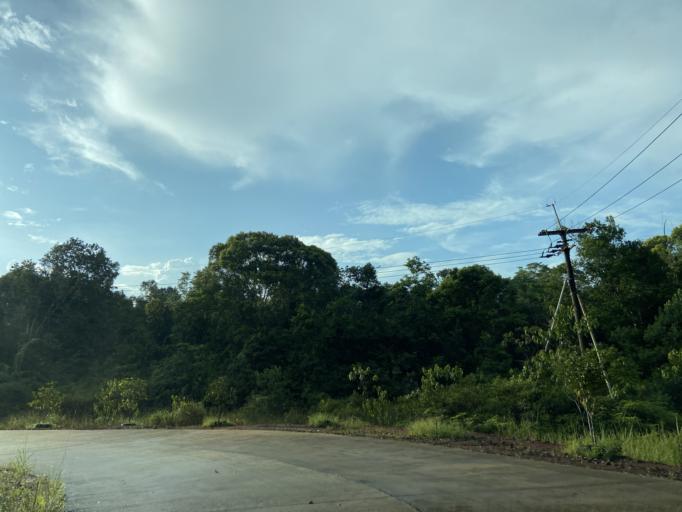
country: ID
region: Riau Islands
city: Tanjungpinang
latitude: 0.8986
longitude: 104.1304
